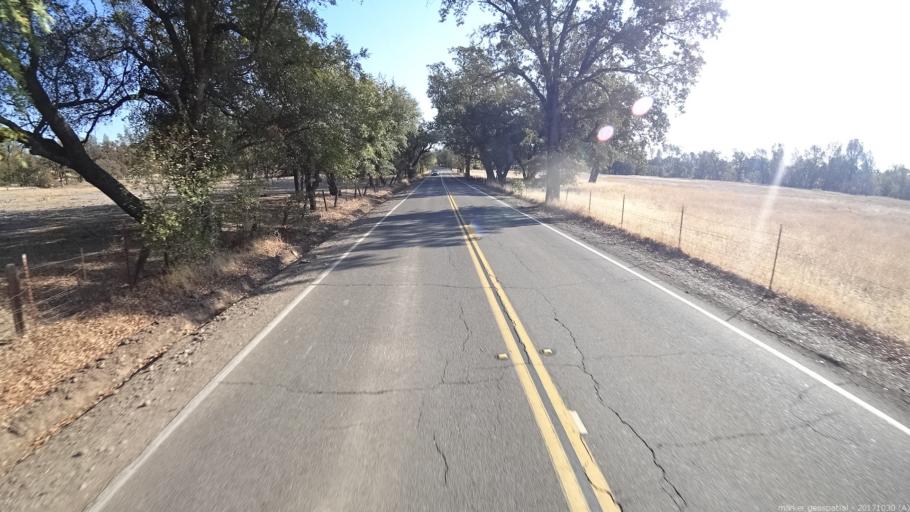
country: US
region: California
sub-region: Shasta County
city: Palo Cedro
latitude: 40.5663
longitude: -122.2104
